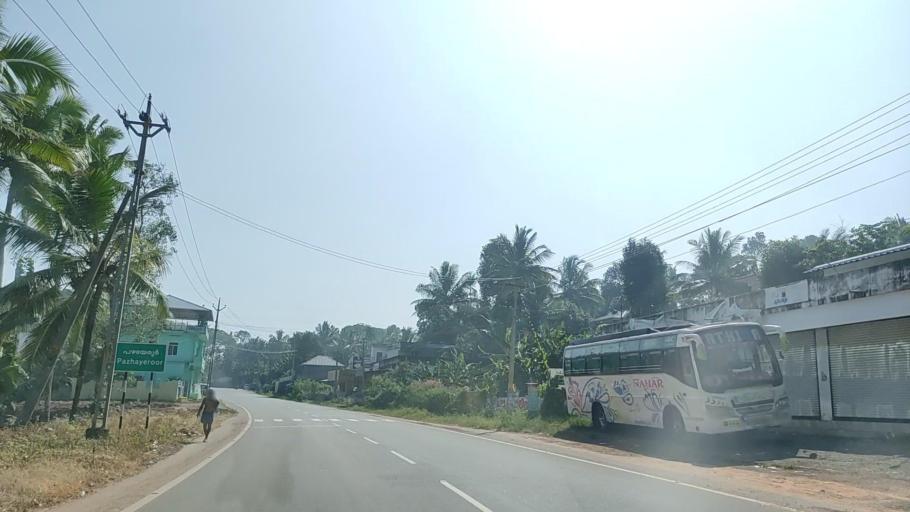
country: IN
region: Kerala
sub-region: Kollam
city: Punalur
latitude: 8.9290
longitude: 76.9727
